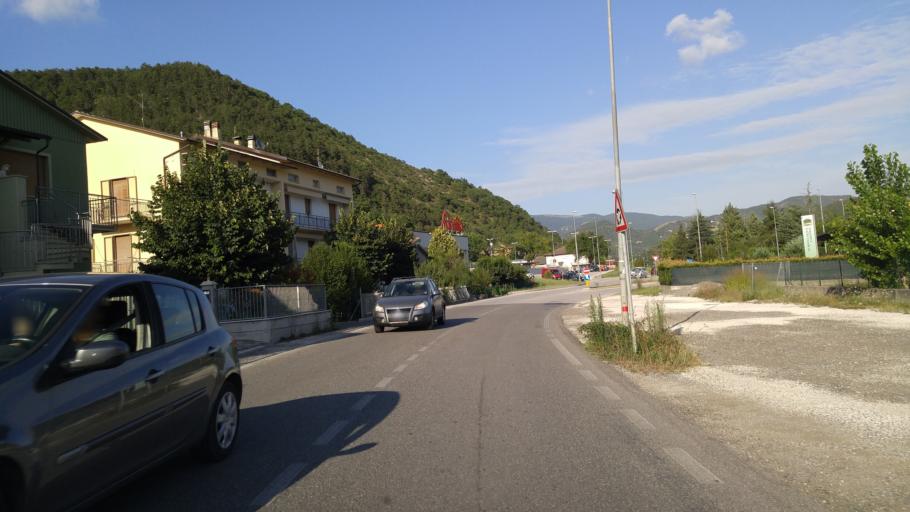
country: IT
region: The Marches
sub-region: Provincia di Pesaro e Urbino
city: Acqualagna
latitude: 43.6149
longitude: 12.6577
